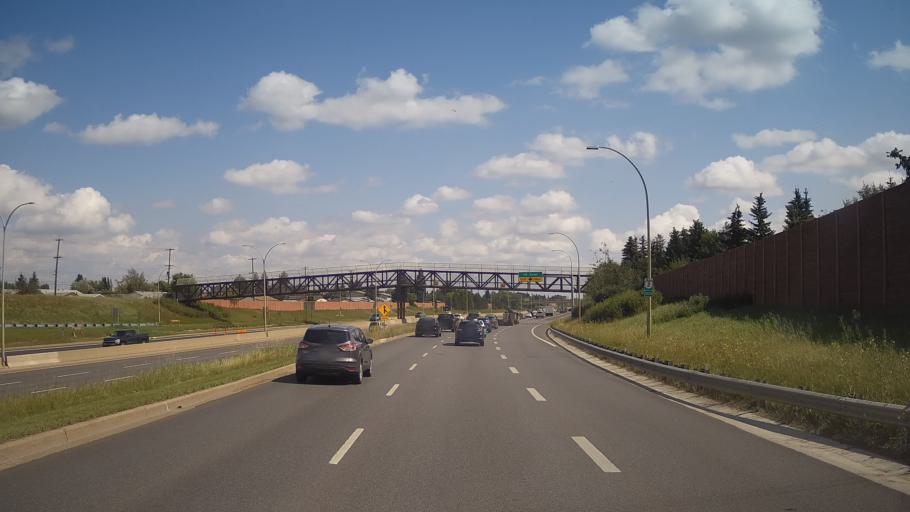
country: CA
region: Alberta
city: St. Albert
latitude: 53.5115
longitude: -113.6128
